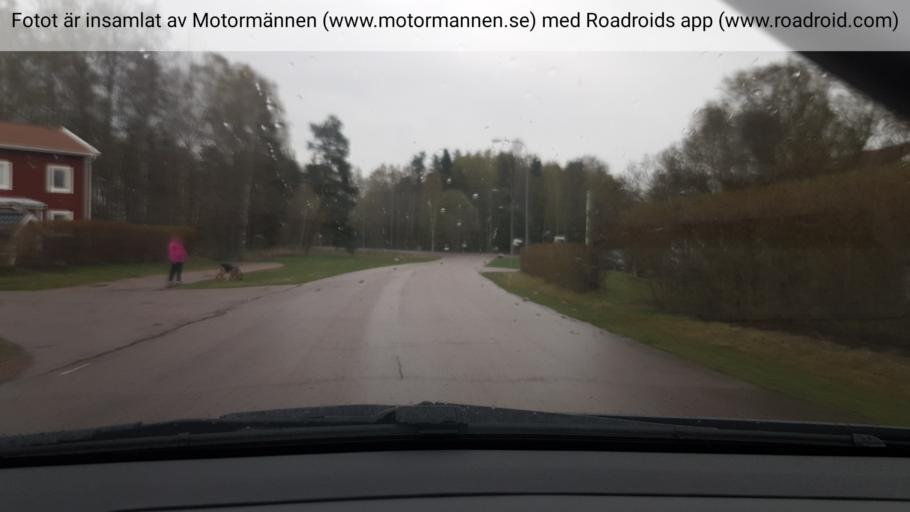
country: SE
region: Dalarna
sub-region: Borlange Kommun
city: Borlaenge
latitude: 60.4812
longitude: 15.3883
